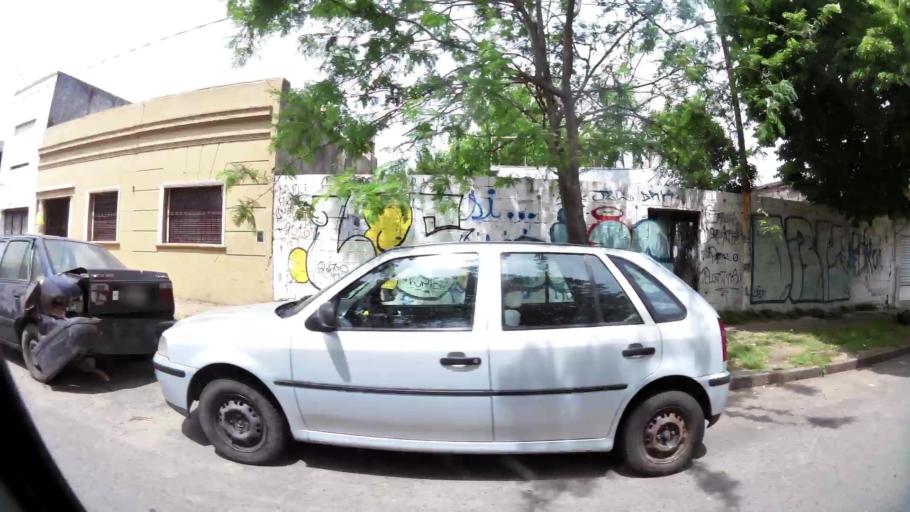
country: AR
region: Buenos Aires
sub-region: Partido de La Plata
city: La Plata
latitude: -34.9440
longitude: -57.9524
